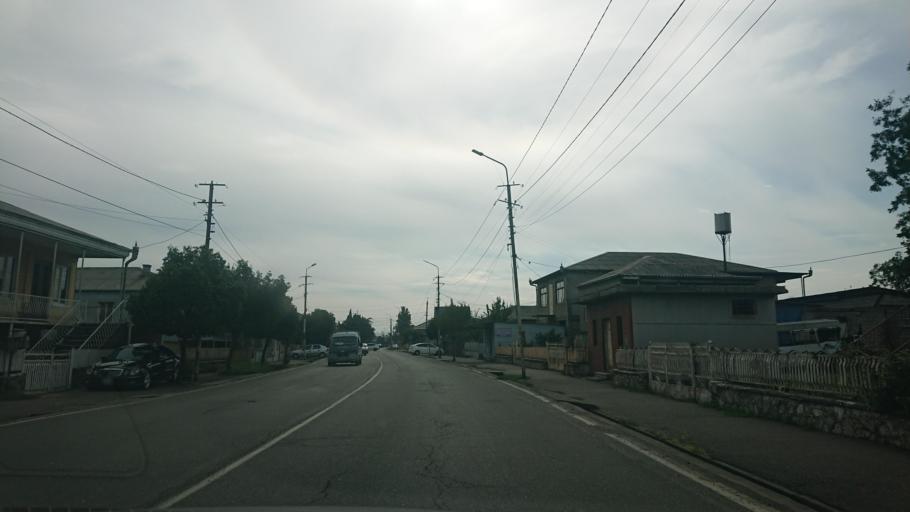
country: GE
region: Samegrelo and Zemo Svaneti
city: P'ot'i
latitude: 42.1591
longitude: 41.6689
